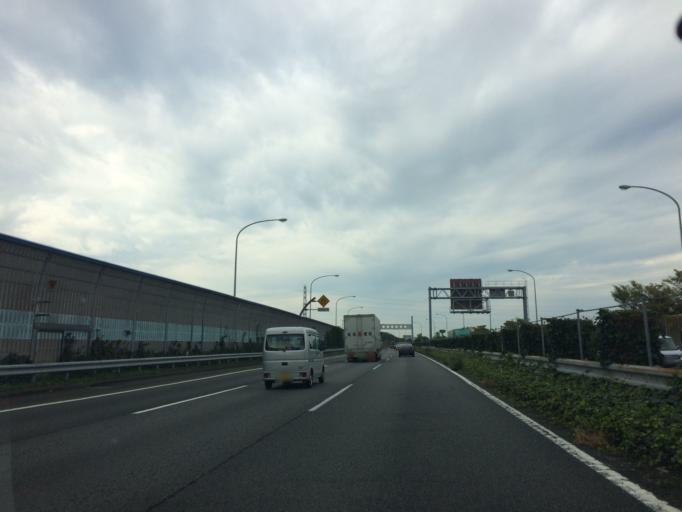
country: JP
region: Shizuoka
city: Yaizu
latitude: 34.8852
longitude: 138.3053
